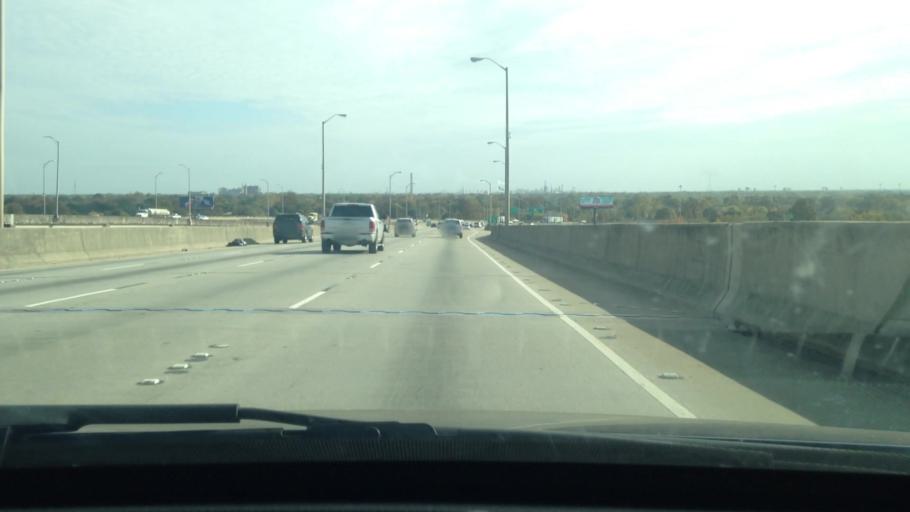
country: US
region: Louisiana
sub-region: Jefferson Parish
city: Gretna
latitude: 29.9378
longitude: -90.0454
